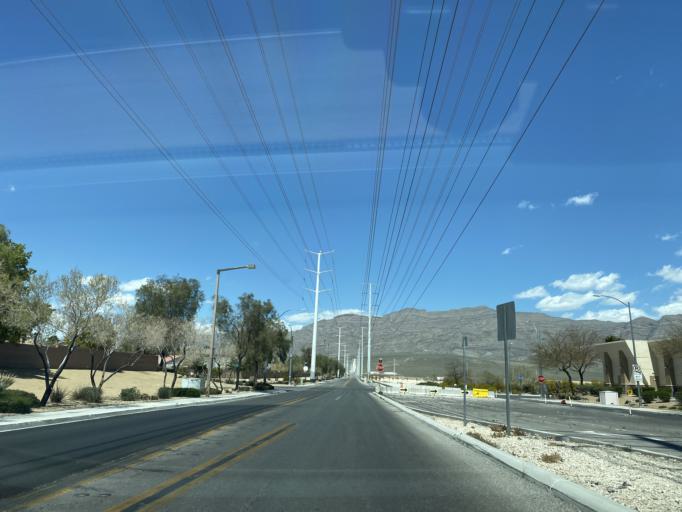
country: US
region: Nevada
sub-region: Clark County
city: North Las Vegas
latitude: 36.3125
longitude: -115.2071
